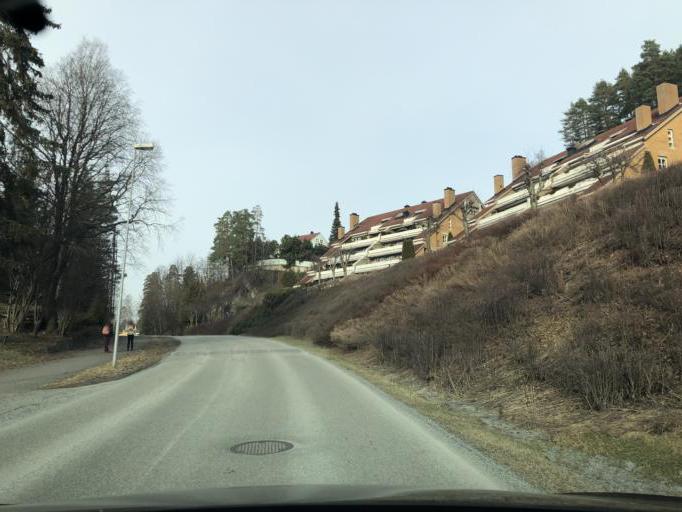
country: NO
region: Akershus
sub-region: Baerum
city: Sandvika
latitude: 59.8662
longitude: 10.5147
